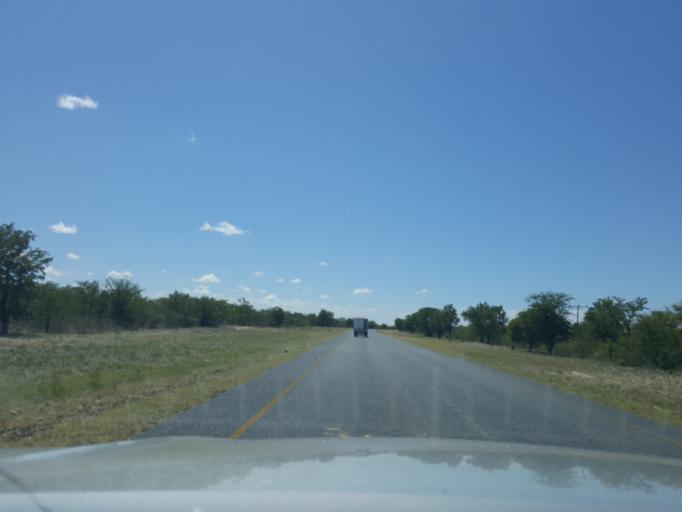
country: BW
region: Central
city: Gweta
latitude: -20.1829
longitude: 25.3046
